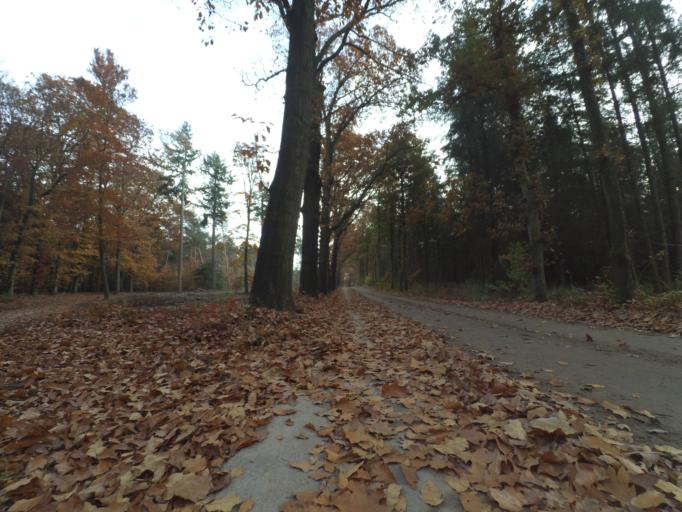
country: NL
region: Gelderland
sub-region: Gemeente Renkum
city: Heelsum
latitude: 52.0165
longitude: 5.7502
